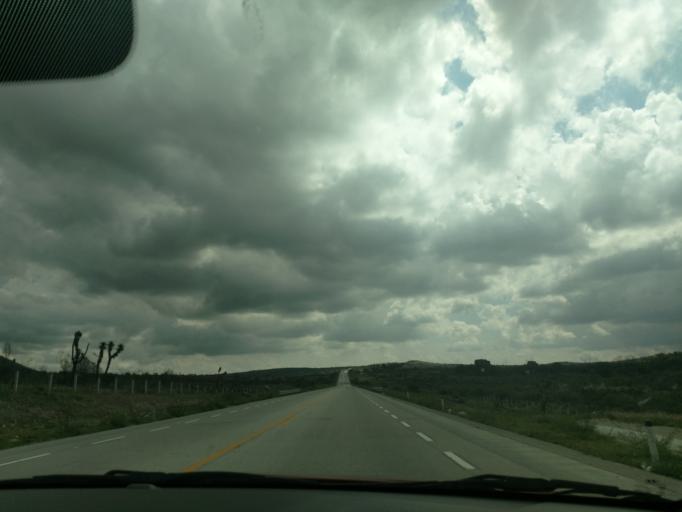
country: MX
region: Jalisco
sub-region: Ojuelos de Jalisco
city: Matanzas
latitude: 21.5580
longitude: -101.6899
